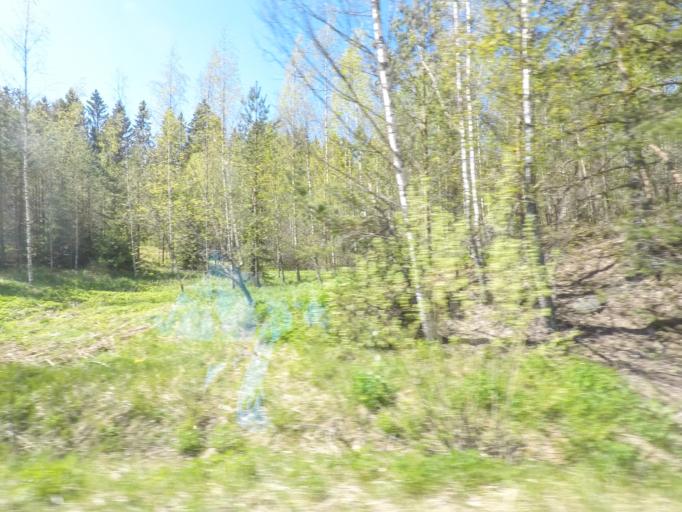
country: FI
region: Uusimaa
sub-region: Helsinki
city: Sammatti
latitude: 60.3502
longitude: 23.7996
